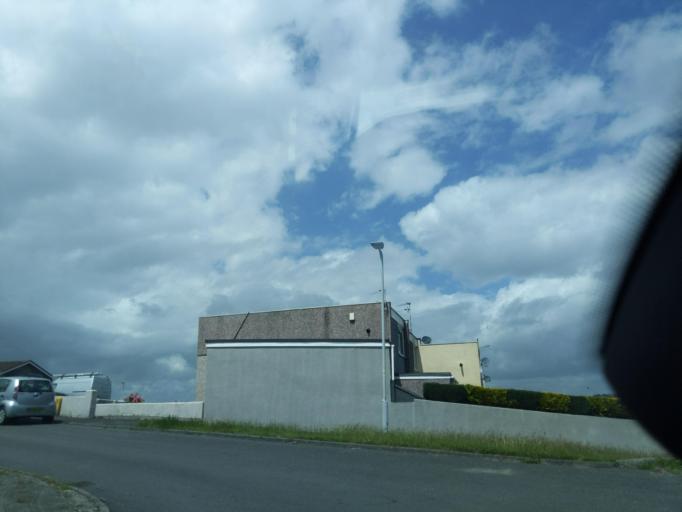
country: GB
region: England
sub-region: Plymouth
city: Plymouth
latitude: 50.4071
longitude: -4.1515
